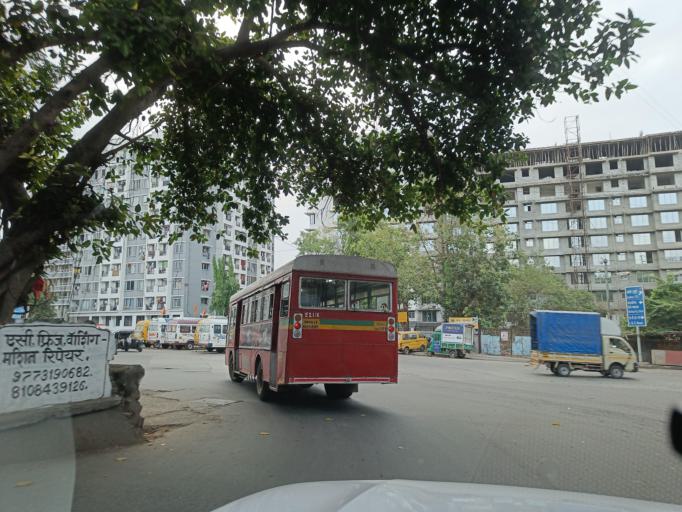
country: IN
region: Maharashtra
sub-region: Mumbai Suburban
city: Powai
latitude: 19.0912
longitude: 72.9074
